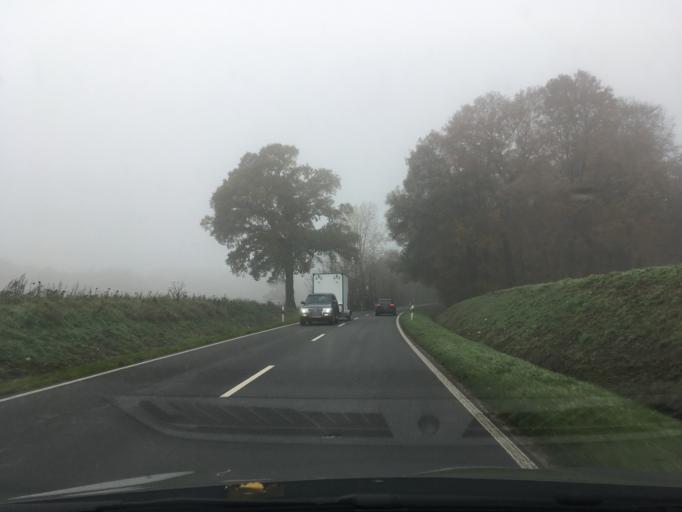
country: DE
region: North Rhine-Westphalia
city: Stadtlohn
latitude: 52.0549
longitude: 6.9434
